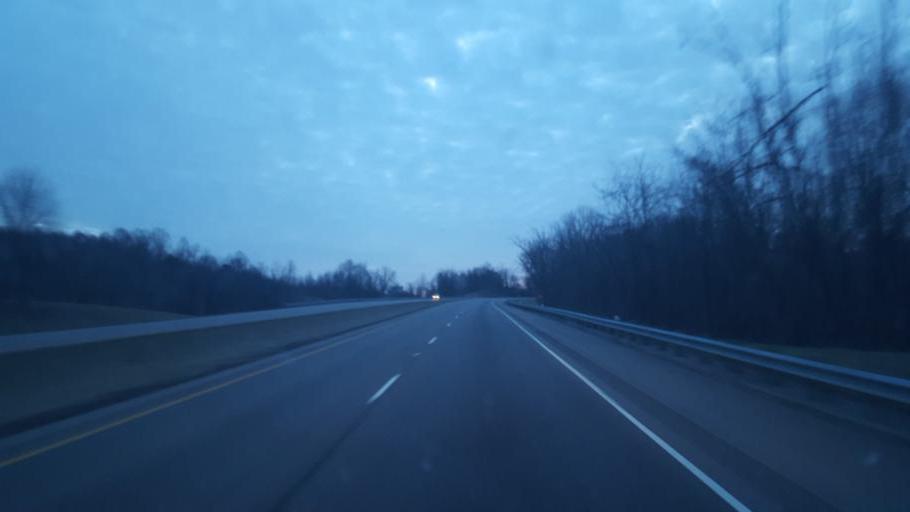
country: US
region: Ohio
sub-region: Jackson County
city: Oak Hill
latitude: 38.9678
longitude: -82.5023
